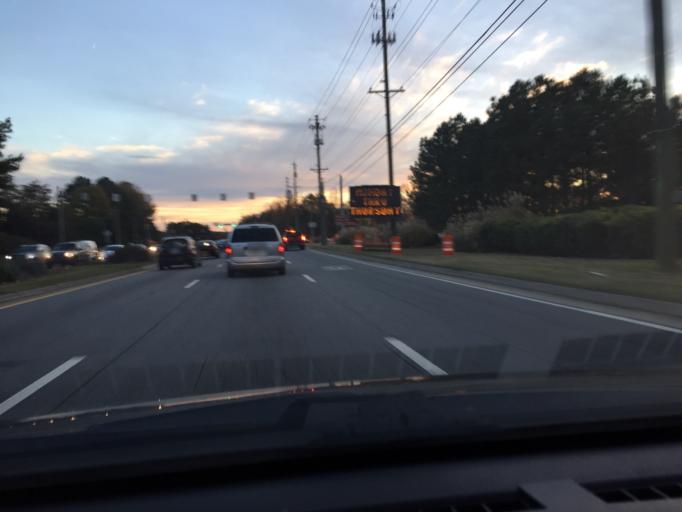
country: US
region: Georgia
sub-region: Fulton County
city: Johns Creek
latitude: 34.0125
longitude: -84.1919
